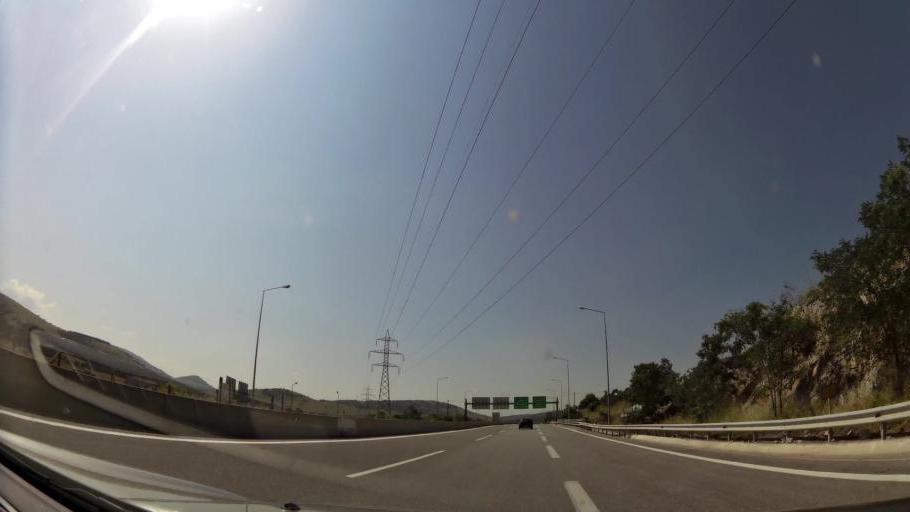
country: GR
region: West Macedonia
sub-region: Nomos Kozanis
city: Koila
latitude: 40.3489
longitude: 21.8048
